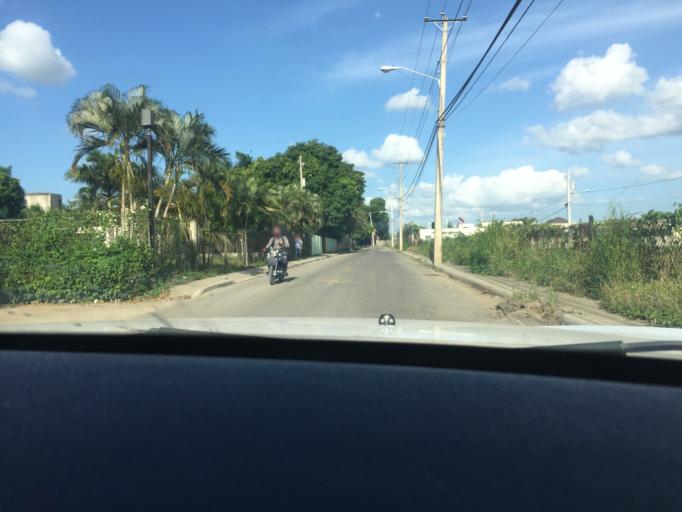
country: DO
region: Santiago
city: Tamboril
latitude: 19.4847
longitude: -70.6543
